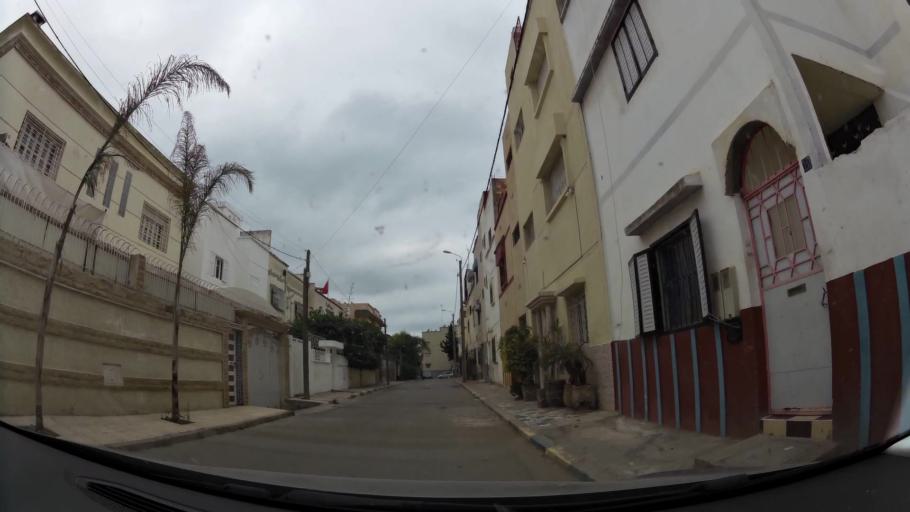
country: MA
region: Rabat-Sale-Zemmour-Zaer
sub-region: Rabat
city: Rabat
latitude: 33.9706
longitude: -6.8180
